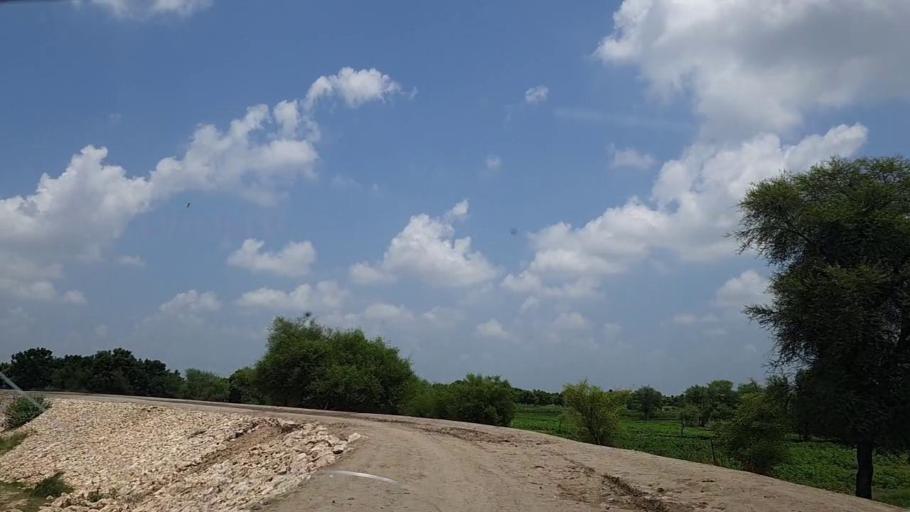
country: PK
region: Sindh
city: Tharu Shah
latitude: 26.9380
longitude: 68.0111
